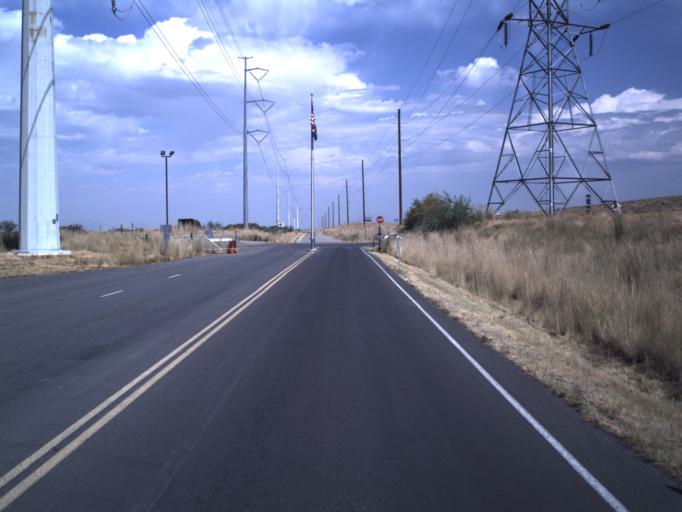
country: US
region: Utah
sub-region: Box Elder County
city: Willard
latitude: 41.4206
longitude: -112.0534
